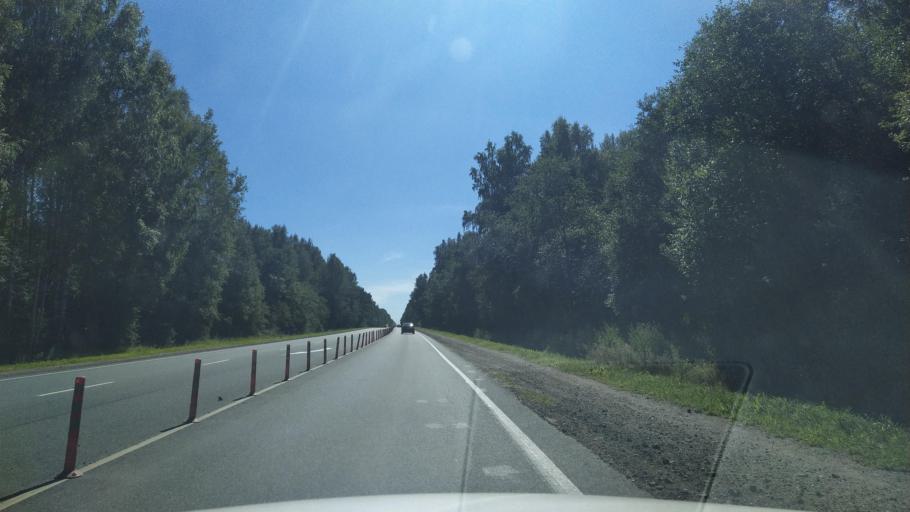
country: RU
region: Pskov
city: Pskov
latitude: 57.7298
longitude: 28.3566
